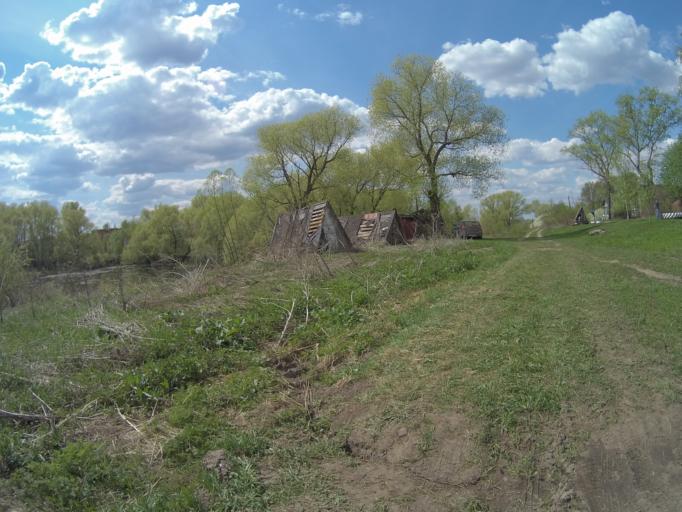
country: RU
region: Vladimir
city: Suzdal'
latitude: 56.3311
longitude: 40.3653
